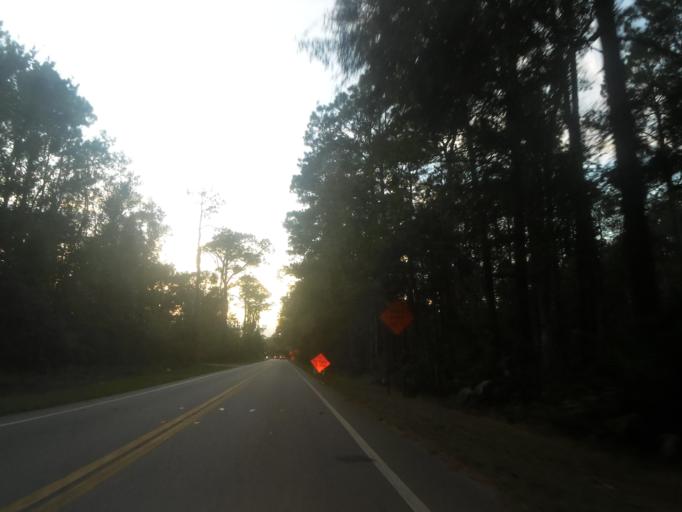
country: US
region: Florida
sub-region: Saint Johns County
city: Fruit Cove
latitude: 30.1045
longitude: -81.5108
